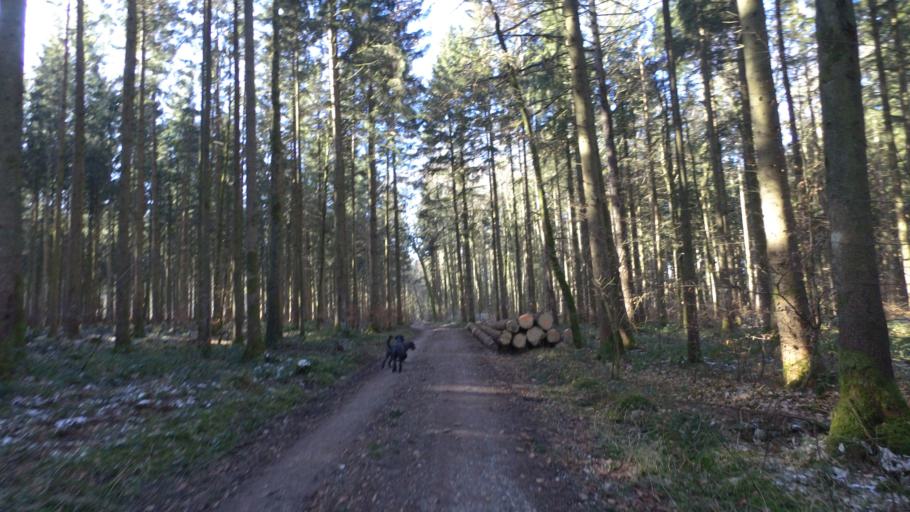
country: DE
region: Bavaria
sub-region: Upper Bavaria
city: Nussdorf
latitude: 47.9270
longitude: 12.5646
